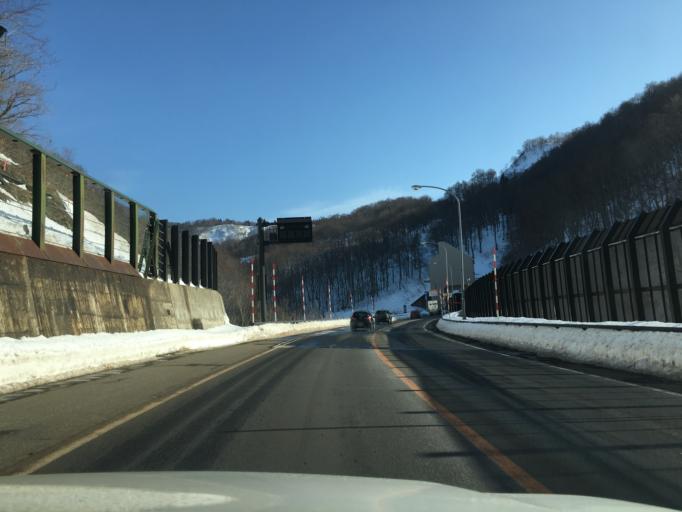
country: JP
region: Yamagata
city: Tsuruoka
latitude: 38.5561
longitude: 139.9301
